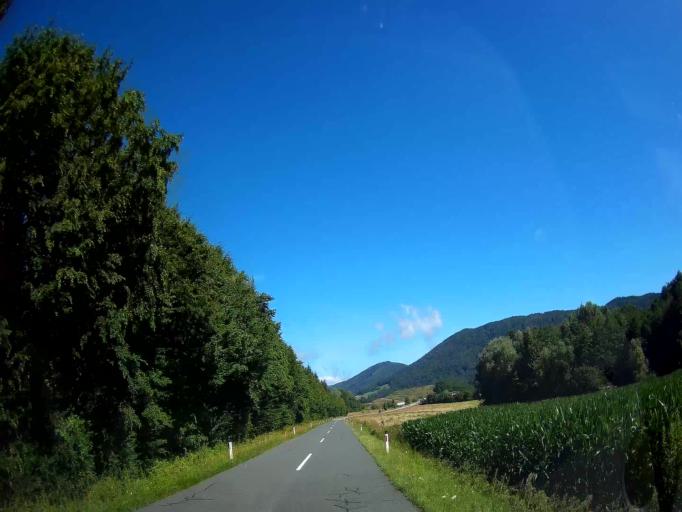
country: AT
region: Carinthia
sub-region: Politischer Bezirk Volkermarkt
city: Voelkermarkt
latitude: 46.6419
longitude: 14.5494
